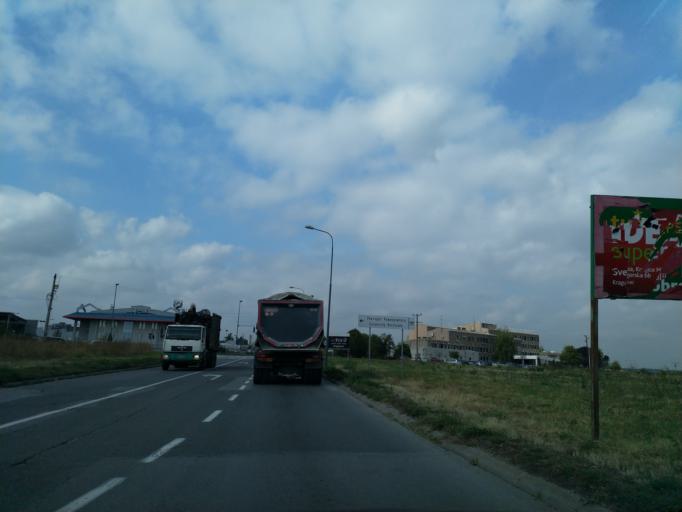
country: RS
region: Central Serbia
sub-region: Sumadijski Okrug
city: Kragujevac
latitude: 44.0272
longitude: 20.9219
